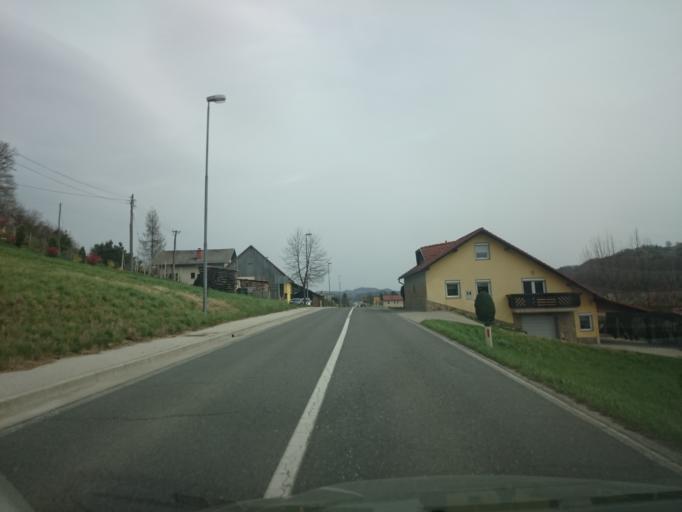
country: SI
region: Sentjur pri Celju
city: Sentjur
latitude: 46.2188
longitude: 15.3585
